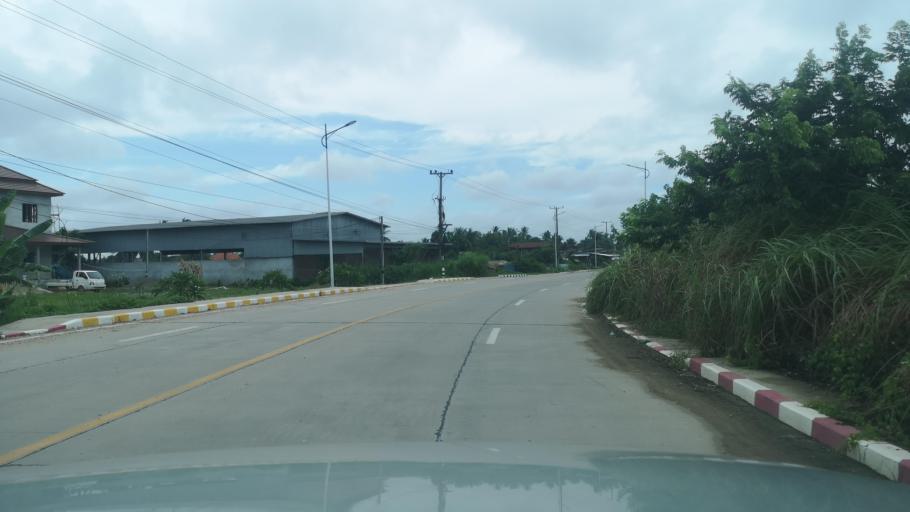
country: TH
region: Nong Khai
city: Tha Bo
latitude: 17.8213
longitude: 102.6637
